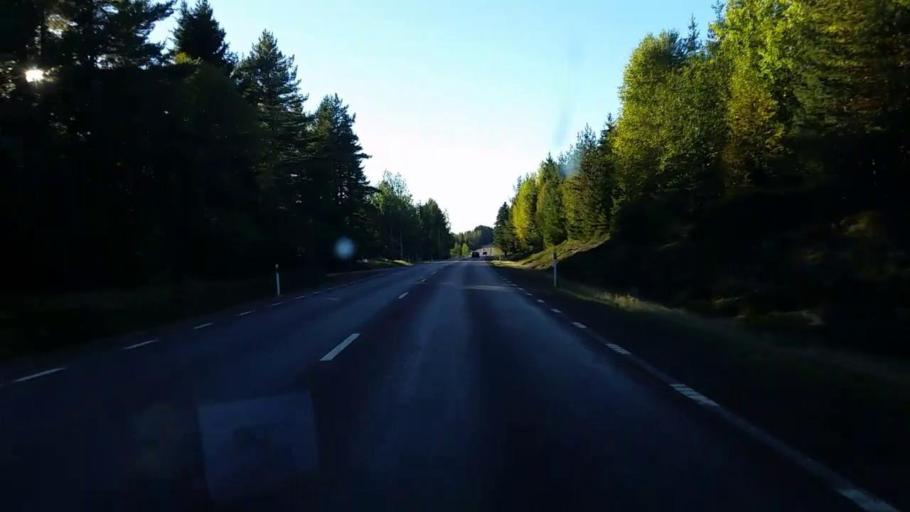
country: SE
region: Gaevleborg
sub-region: Ljusdals Kommun
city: Jaervsoe
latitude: 61.8052
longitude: 16.2581
